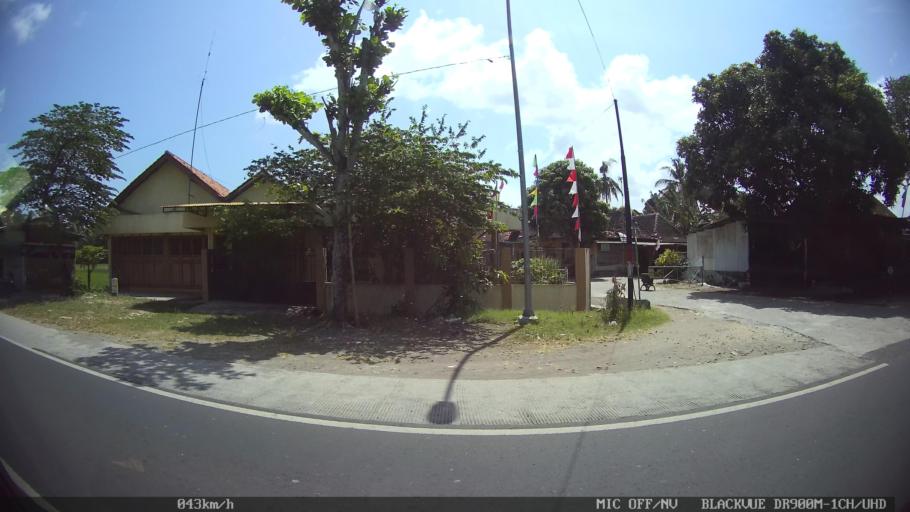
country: ID
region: Daerah Istimewa Yogyakarta
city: Pundong
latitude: -7.9219
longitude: 110.3753
